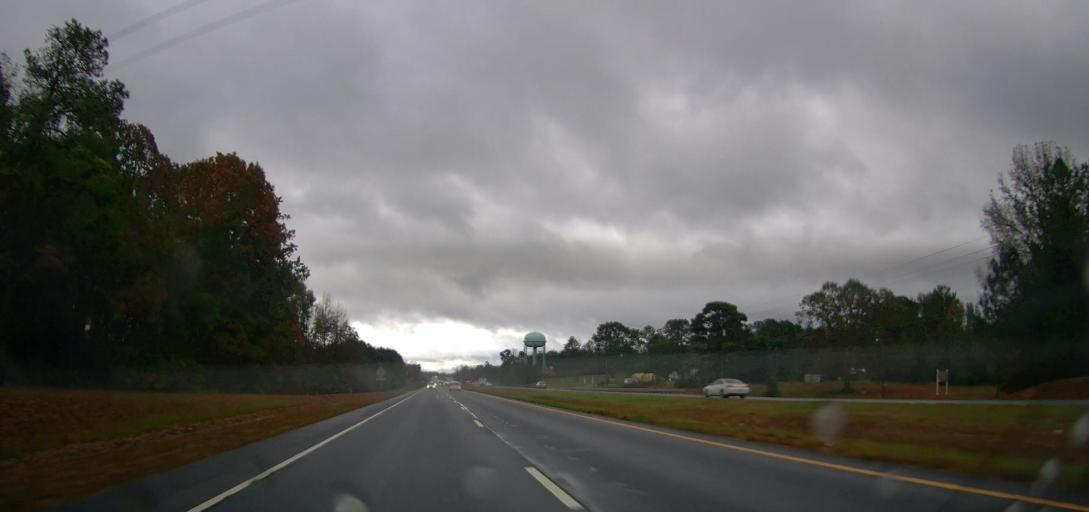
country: US
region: Georgia
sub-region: Jackson County
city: Nicholson
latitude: 34.1437
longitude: -83.4355
